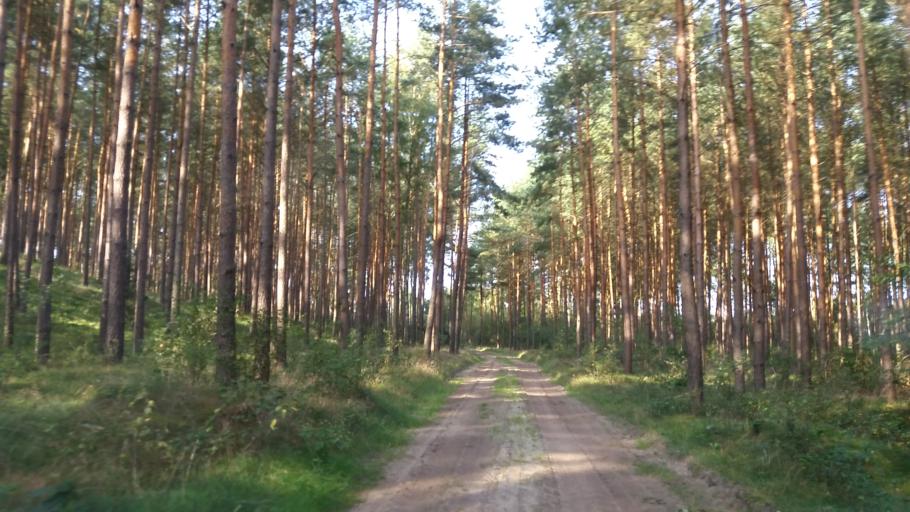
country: PL
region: West Pomeranian Voivodeship
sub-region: Powiat choszczenski
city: Choszczno
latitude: 53.2439
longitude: 15.3974
